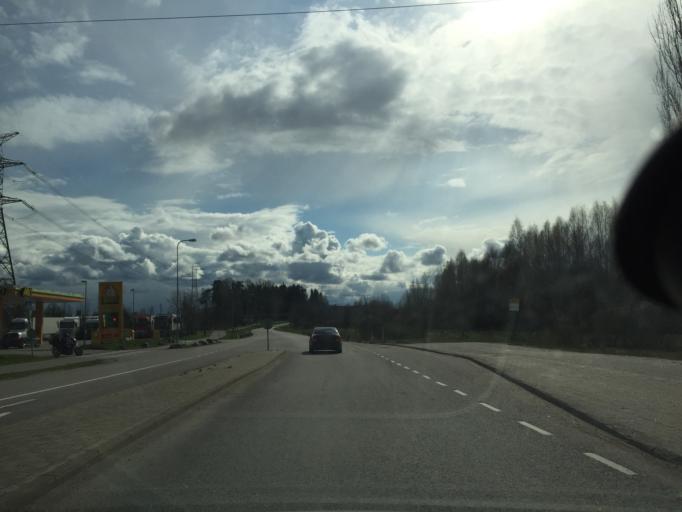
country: FI
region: Uusimaa
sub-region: Helsinki
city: Kilo
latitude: 60.2851
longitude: 24.8268
